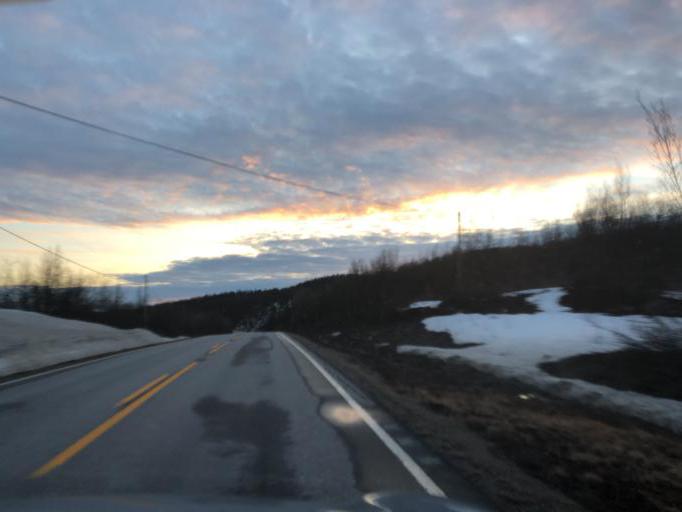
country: NO
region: Sor-Trondelag
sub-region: Tydal
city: Aas
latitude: 62.6358
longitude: 11.9546
